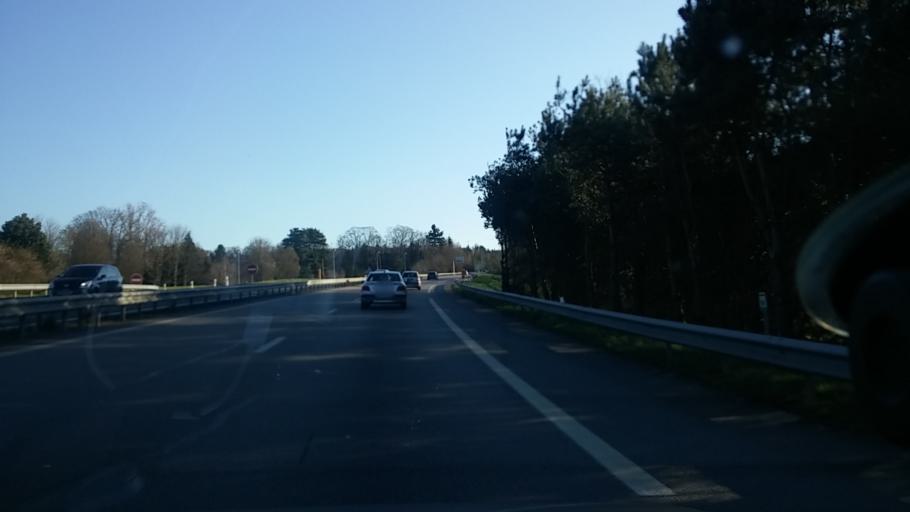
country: FR
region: Limousin
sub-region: Departement de la Haute-Vienne
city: Bessines-sur-Gartempe
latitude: 46.1112
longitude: 1.3752
